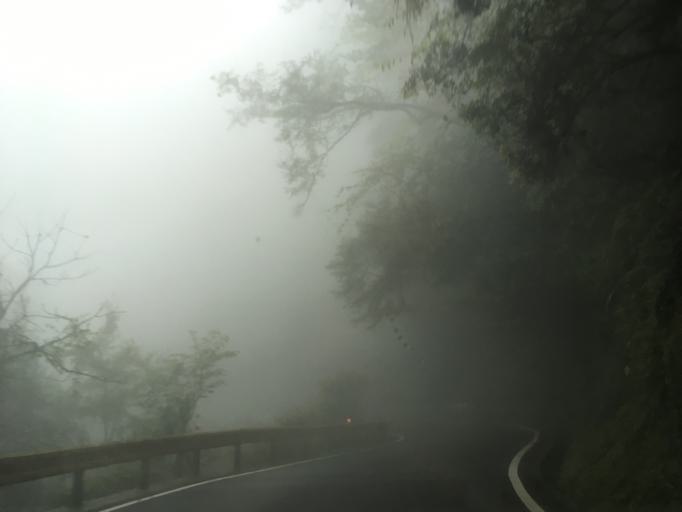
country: TW
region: Taiwan
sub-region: Hualien
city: Hualian
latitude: 24.1952
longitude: 121.4218
